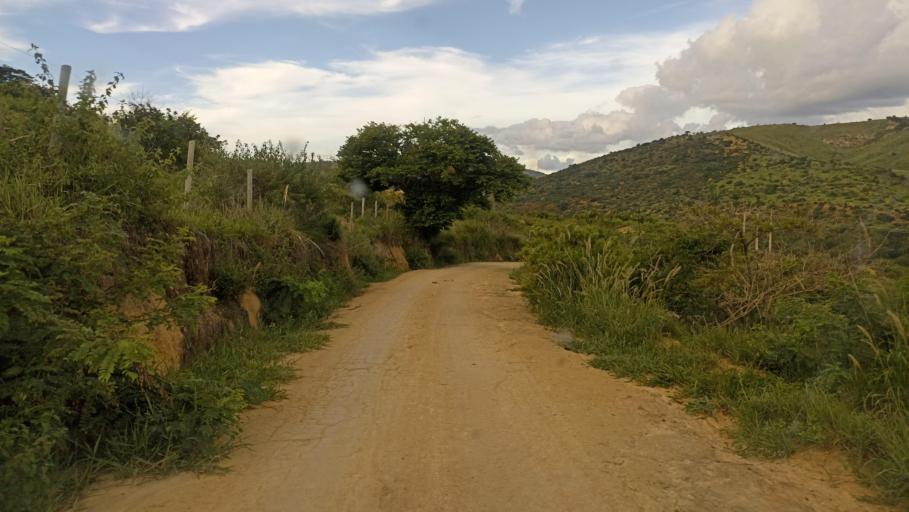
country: BR
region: Minas Gerais
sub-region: Almenara
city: Almenara
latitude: -16.5393
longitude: -40.4456
